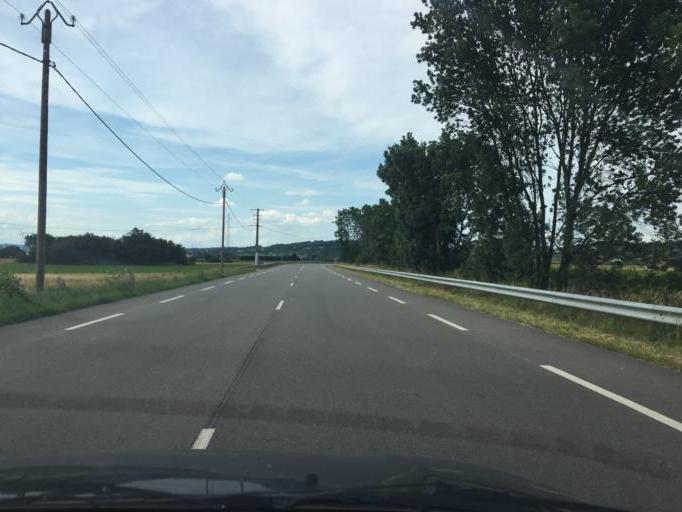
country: FR
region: Rhone-Alpes
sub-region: Departement de la Drome
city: Beaumont-Monteux
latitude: 45.0384
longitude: 4.9312
